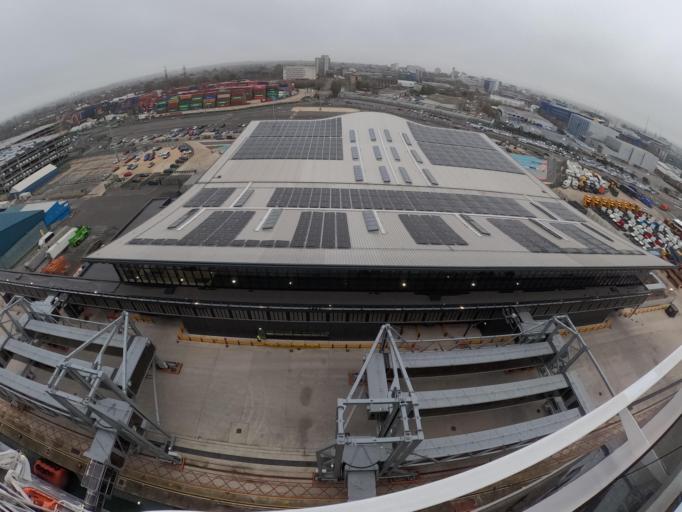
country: GB
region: England
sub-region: Southampton
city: Southampton
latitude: 50.9015
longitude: -1.4195
